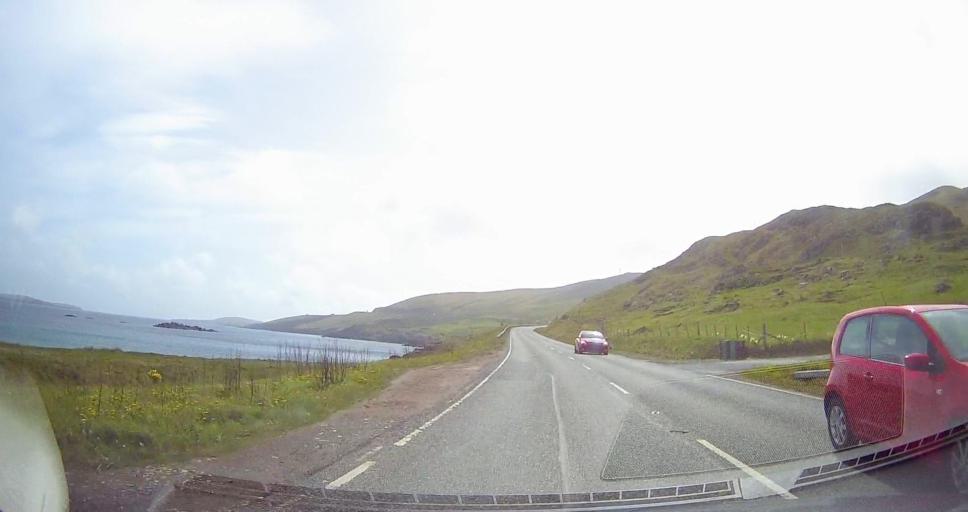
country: GB
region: Scotland
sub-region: Shetland Islands
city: Sandwick
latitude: 60.0346
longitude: -1.2329
